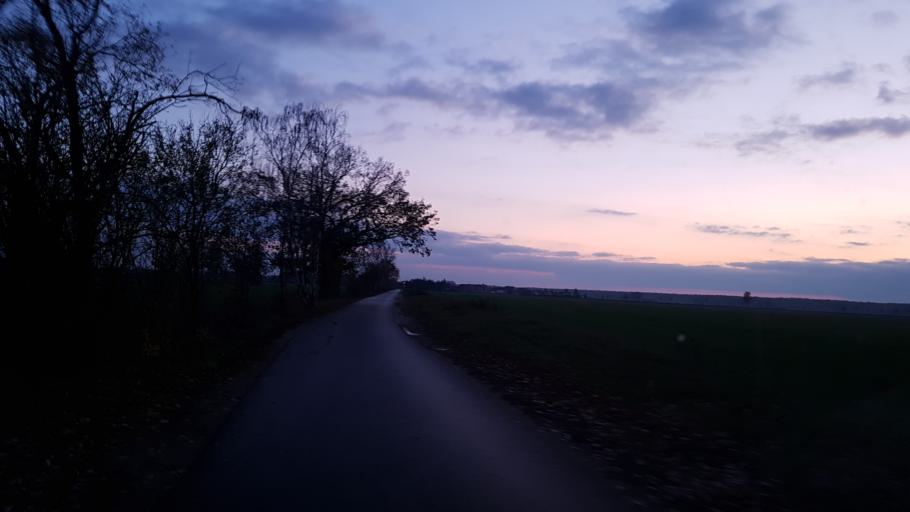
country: DE
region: Brandenburg
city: Herzberg
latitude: 51.6322
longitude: 13.2046
